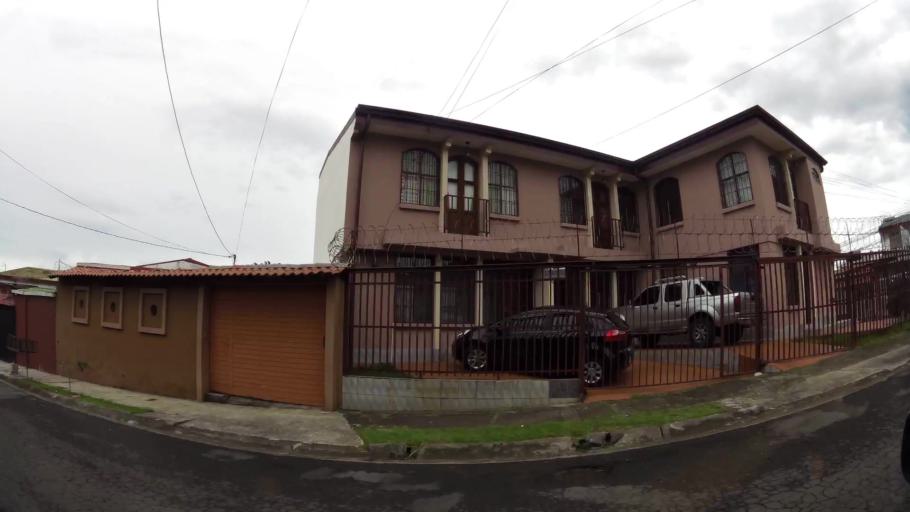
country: CR
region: San Jose
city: Calle Blancos
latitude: 9.9522
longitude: -84.0644
